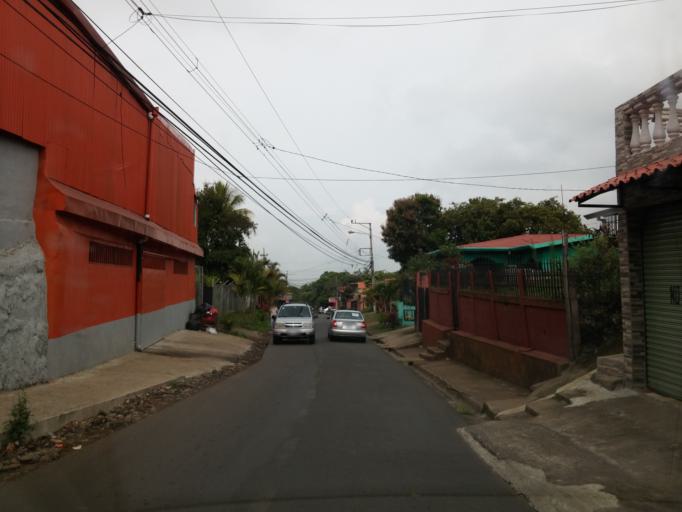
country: CR
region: Heredia
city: Llorente
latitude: 10.0158
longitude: -84.1681
